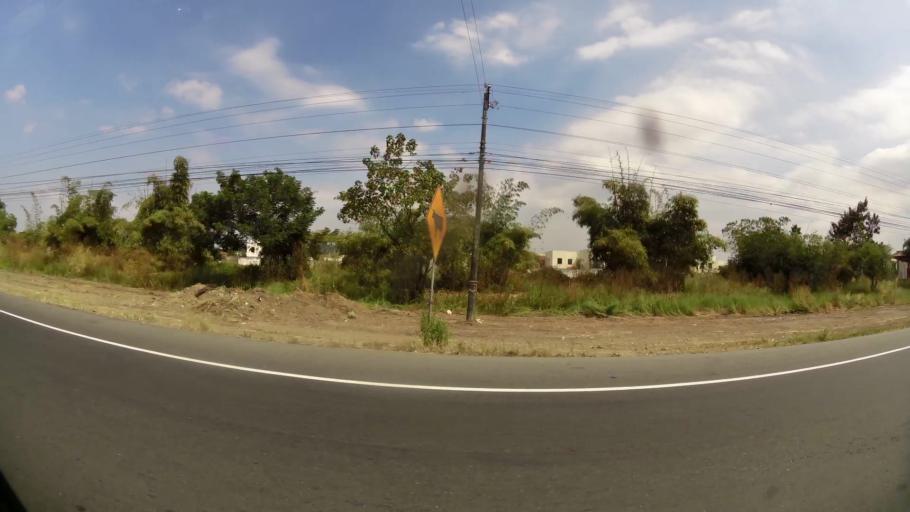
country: EC
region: Guayas
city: Eloy Alfaro
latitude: -2.0507
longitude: -79.9013
